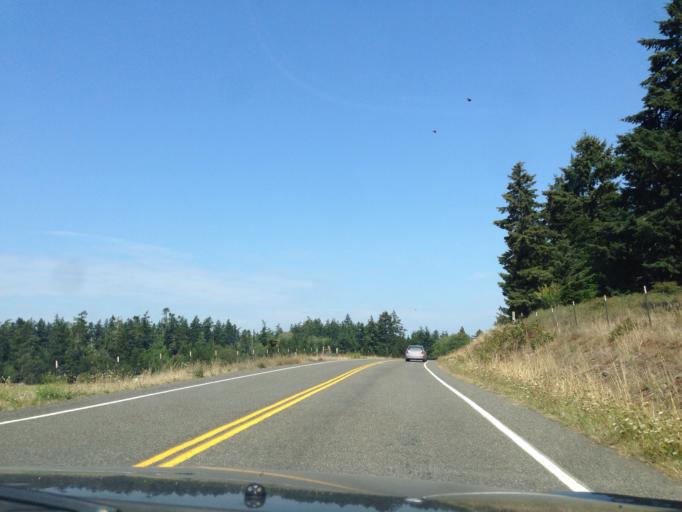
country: US
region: Washington
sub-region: San Juan County
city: Friday Harbor
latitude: 48.4939
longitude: -123.0325
